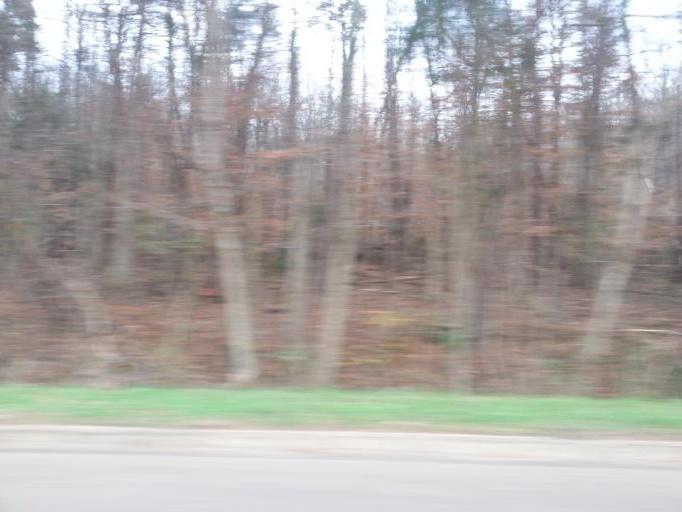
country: US
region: Tennessee
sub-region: Hamilton County
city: Sale Creek
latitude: 35.4018
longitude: -85.1032
